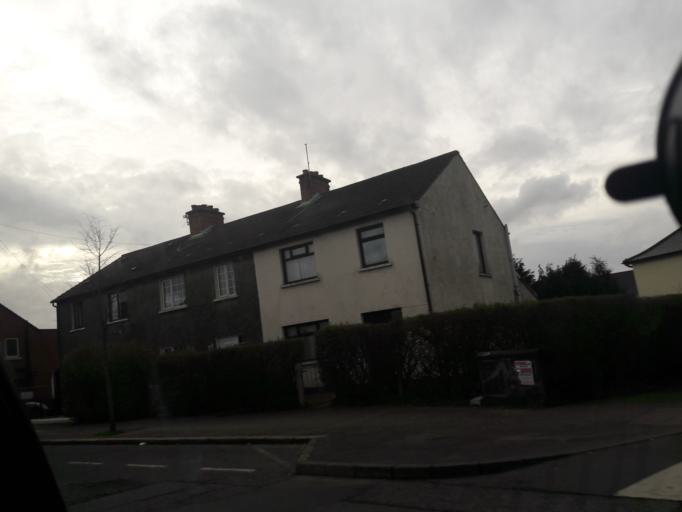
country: GB
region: Northern Ireland
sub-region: City of Belfast
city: Belfast
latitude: 54.6181
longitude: -5.9541
